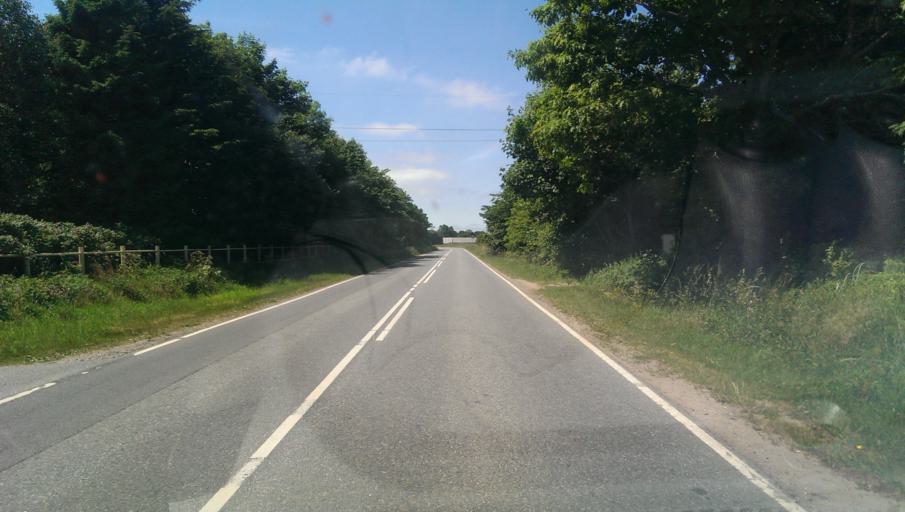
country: DK
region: South Denmark
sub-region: Fano Kommune
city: Nordby
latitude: 55.5321
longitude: 8.3882
